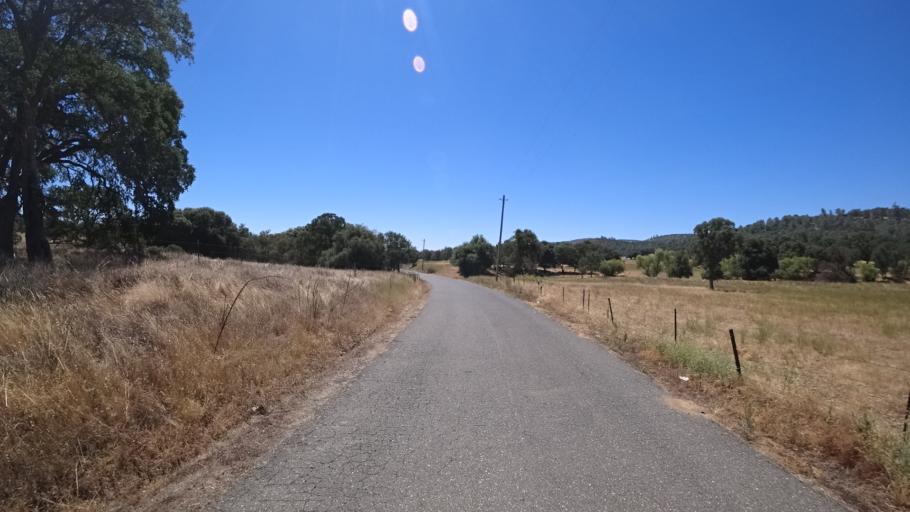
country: US
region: California
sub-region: Calaveras County
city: Copperopolis
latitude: 37.9529
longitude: -120.6857
